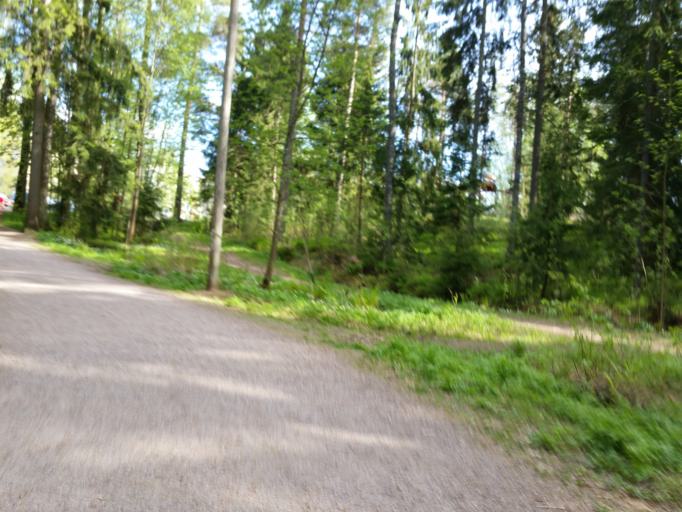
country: FI
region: Uusimaa
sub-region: Helsinki
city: Kauniainen
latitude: 60.1772
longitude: 24.7282
